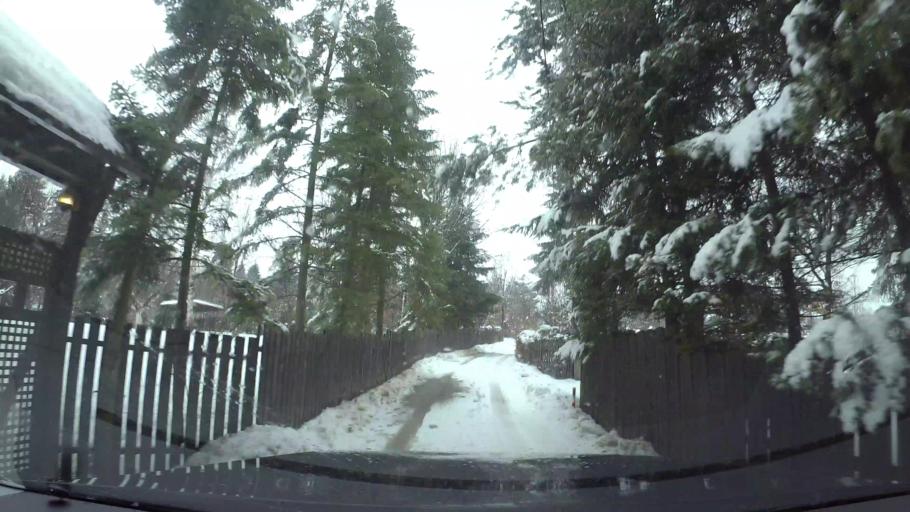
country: BA
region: Federation of Bosnia and Herzegovina
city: Hadzici
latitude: 43.8605
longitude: 18.2641
